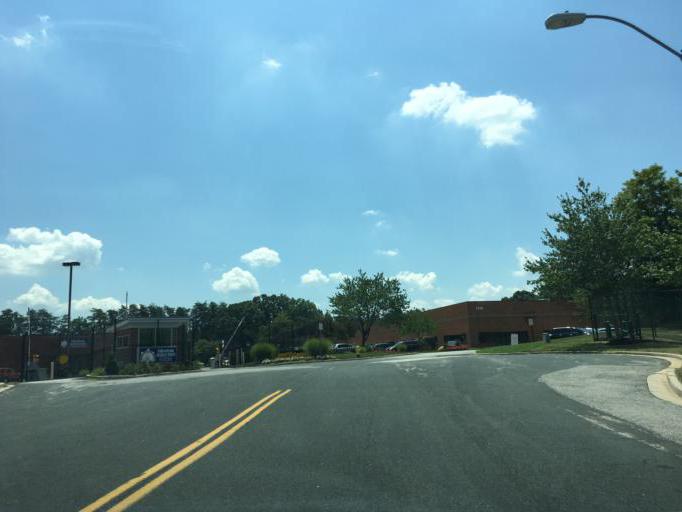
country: US
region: Maryland
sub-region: Howard County
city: Hanover
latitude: 39.1688
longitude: -76.7358
